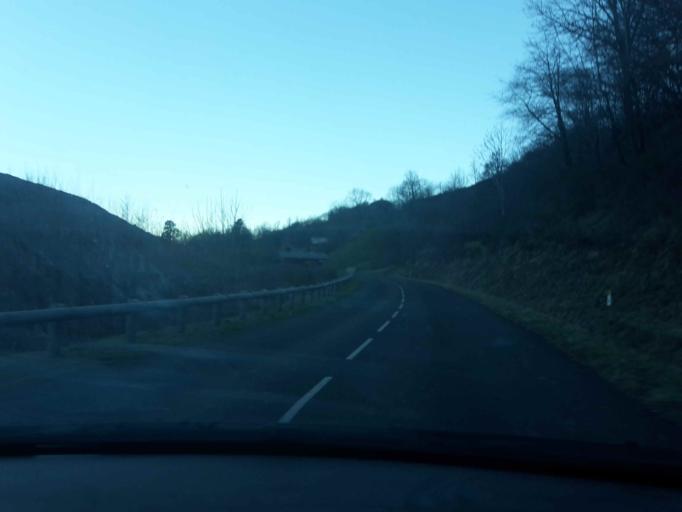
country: FR
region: Auvergne
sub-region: Departement du Cantal
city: Riom-es-Montagnes
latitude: 45.1641
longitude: 2.6093
